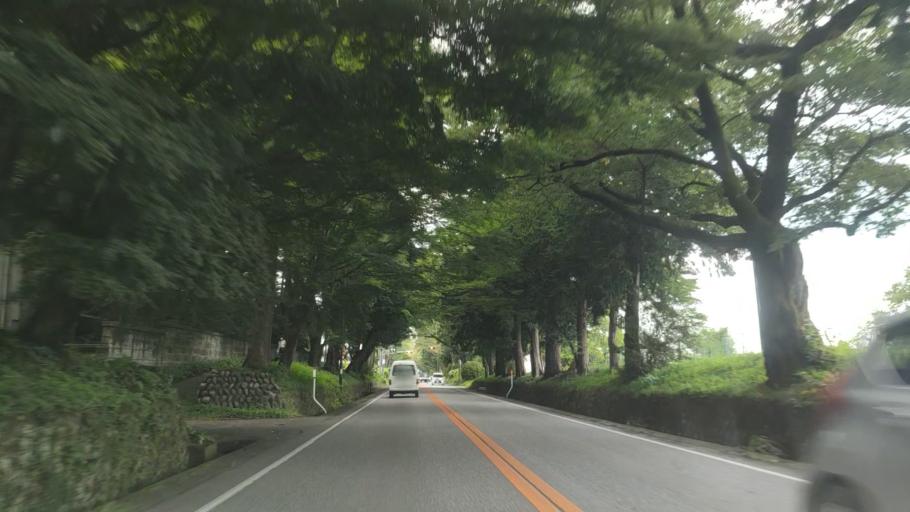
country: JP
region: Tochigi
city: Utsunomiya-shi
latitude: 36.6319
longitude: 139.8509
